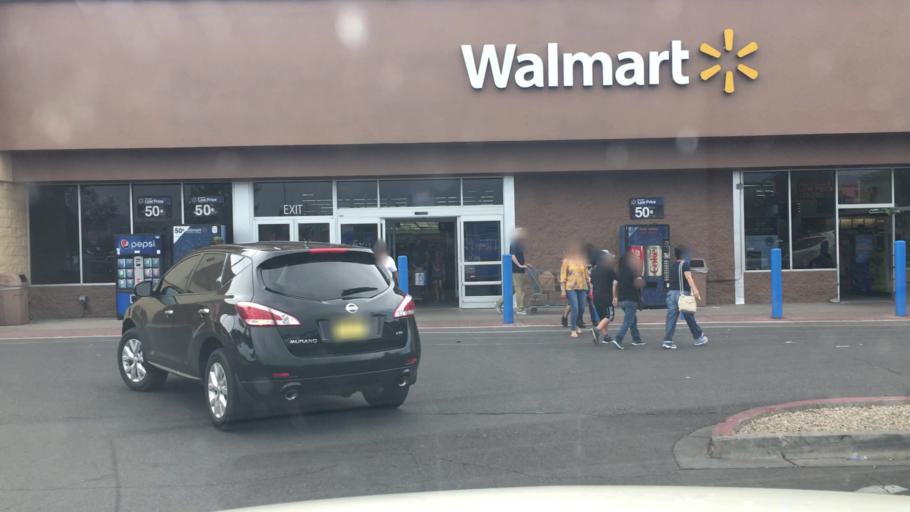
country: US
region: New Mexico
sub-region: Santa Fe County
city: Agua Fria
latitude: 35.6527
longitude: -105.9990
